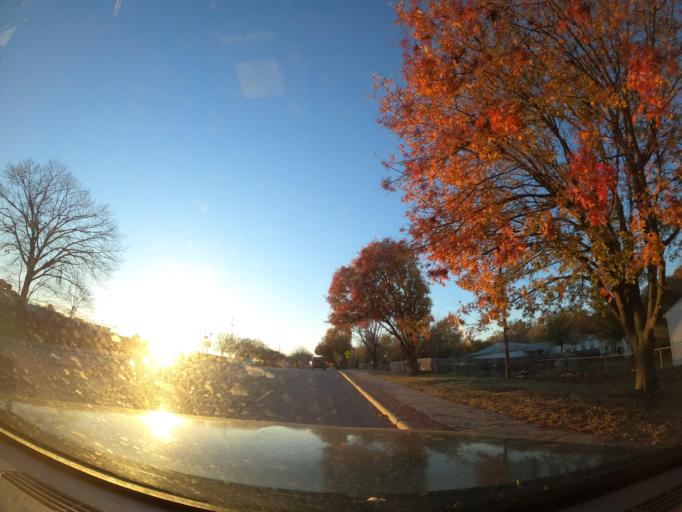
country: US
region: Oklahoma
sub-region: Tulsa County
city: Tulsa
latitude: 36.1406
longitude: -95.9253
